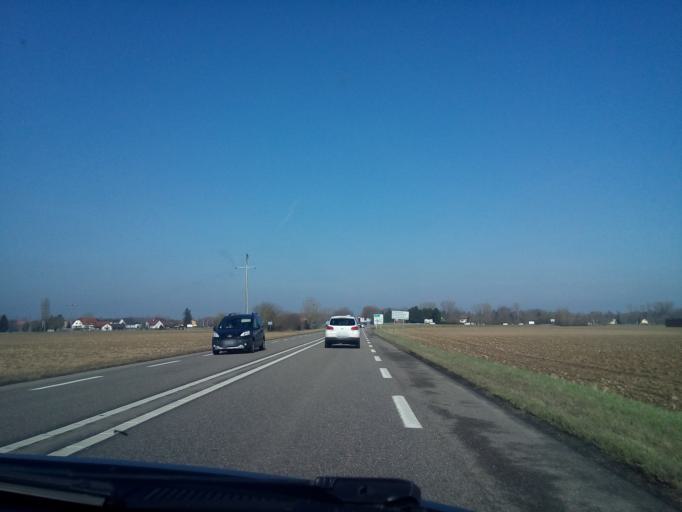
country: FR
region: Alsace
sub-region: Departement du Bas-Rhin
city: Roppenheim
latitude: 48.8451
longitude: 8.0674
